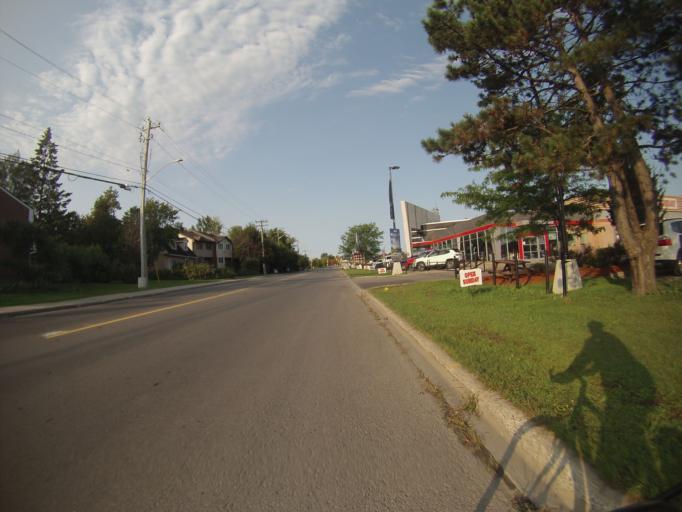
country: CA
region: Ontario
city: Ottawa
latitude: 45.3613
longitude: -75.6548
